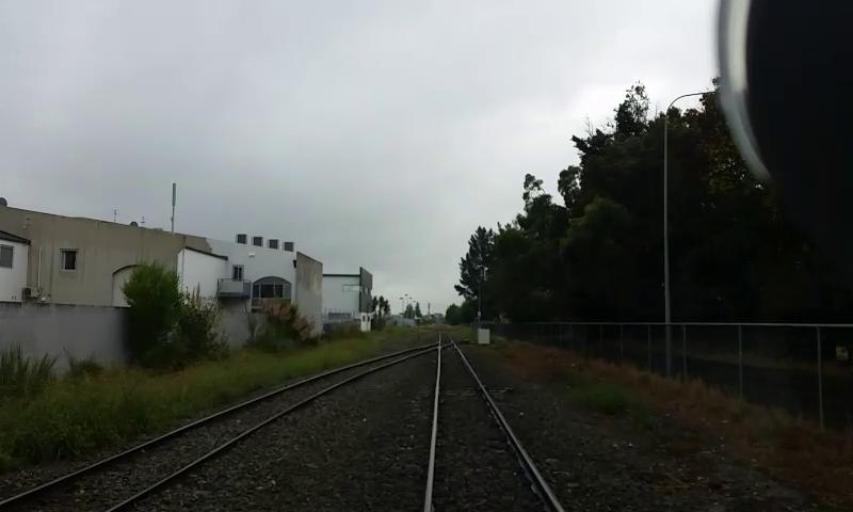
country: NZ
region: Canterbury
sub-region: Christchurch City
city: Christchurch
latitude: -43.5370
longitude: 172.6098
